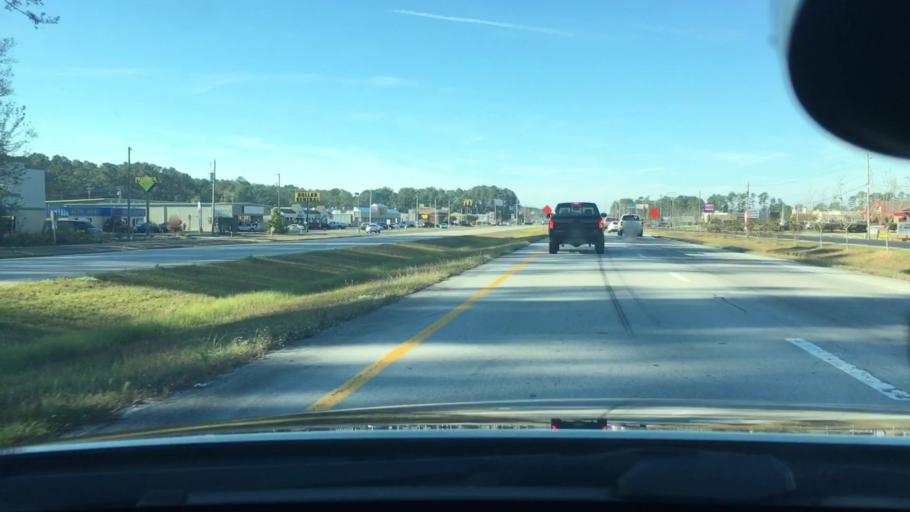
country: US
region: North Carolina
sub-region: Craven County
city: Havelock
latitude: 34.9066
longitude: -76.9344
